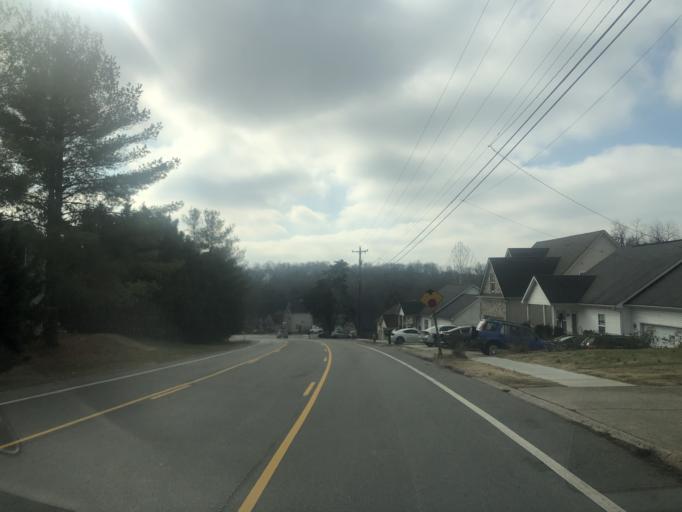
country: US
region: Tennessee
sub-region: Rutherford County
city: La Vergne
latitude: 36.0769
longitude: -86.6473
